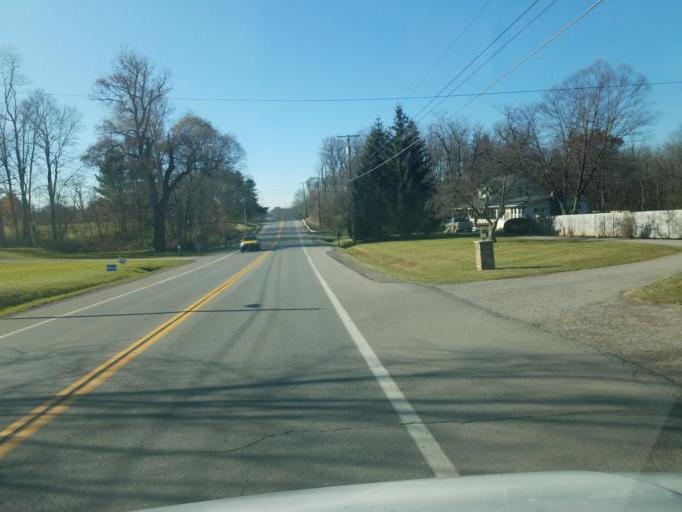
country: US
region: Ohio
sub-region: Ashland County
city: Ashland
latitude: 40.8300
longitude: -82.3783
